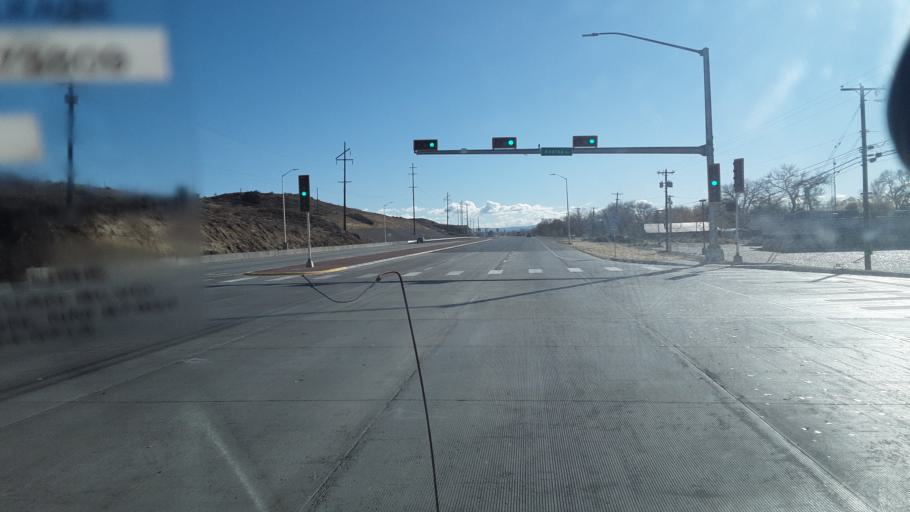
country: US
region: New Mexico
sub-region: San Juan County
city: Farmington
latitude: 36.7099
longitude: -108.1359
